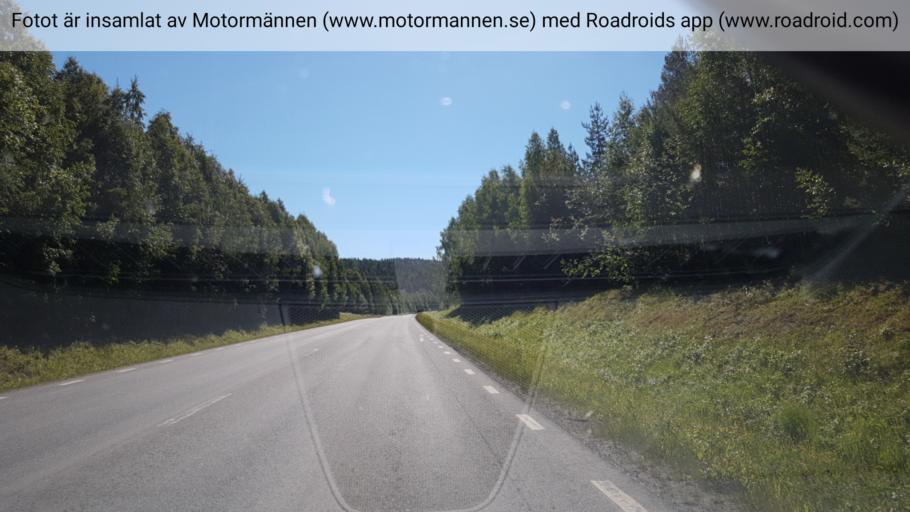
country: SE
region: Norrbotten
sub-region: Bodens Kommun
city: Boden
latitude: 65.8485
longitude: 21.5879
